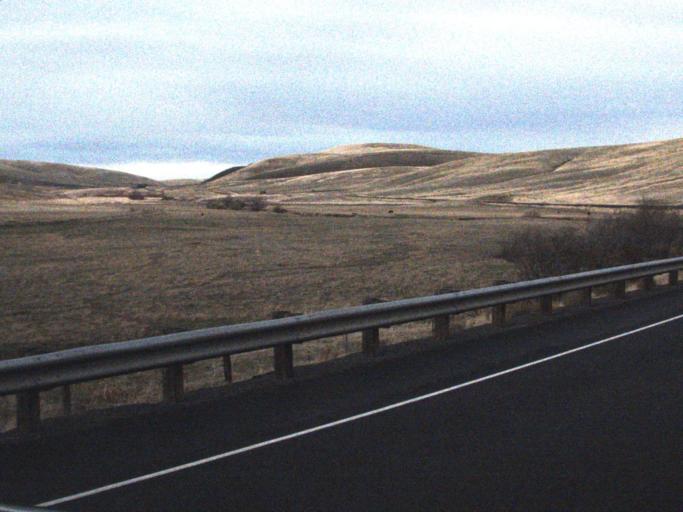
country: US
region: Washington
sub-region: Columbia County
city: Dayton
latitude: 46.5095
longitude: -117.9531
